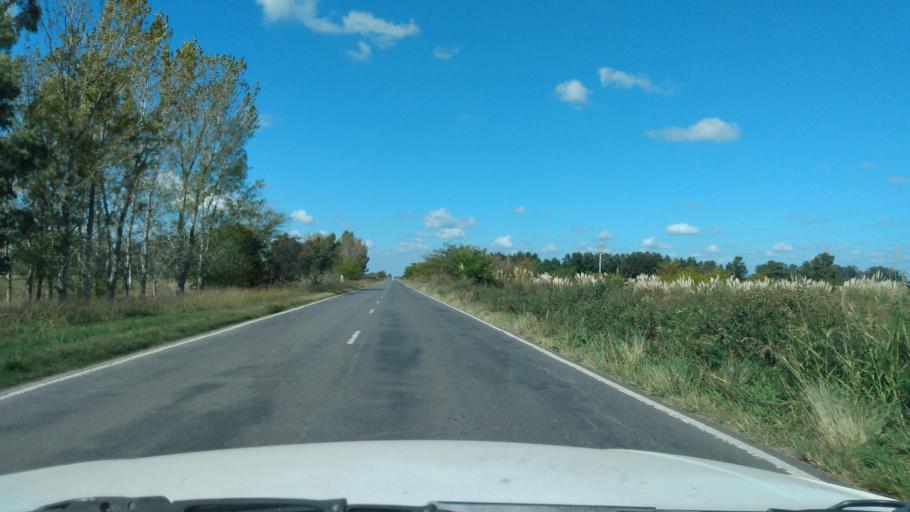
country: AR
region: Buenos Aires
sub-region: Partido de Mercedes
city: Mercedes
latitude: -34.7161
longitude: -59.3967
